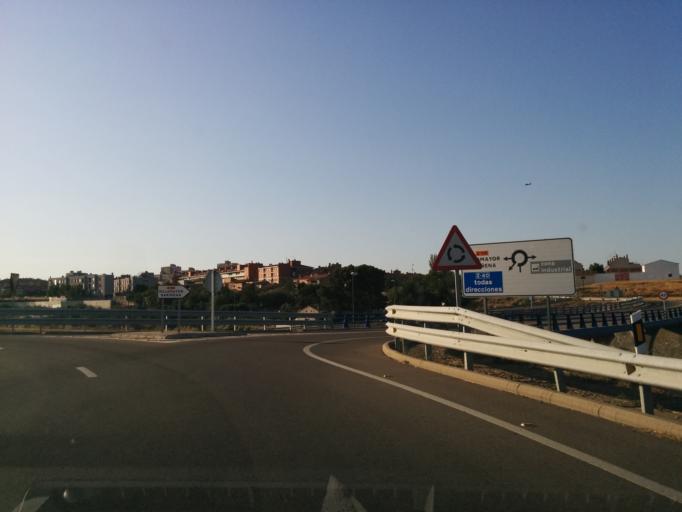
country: ES
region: Aragon
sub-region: Provincia de Zaragoza
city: Zaragoza
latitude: 41.6619
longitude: -0.8220
